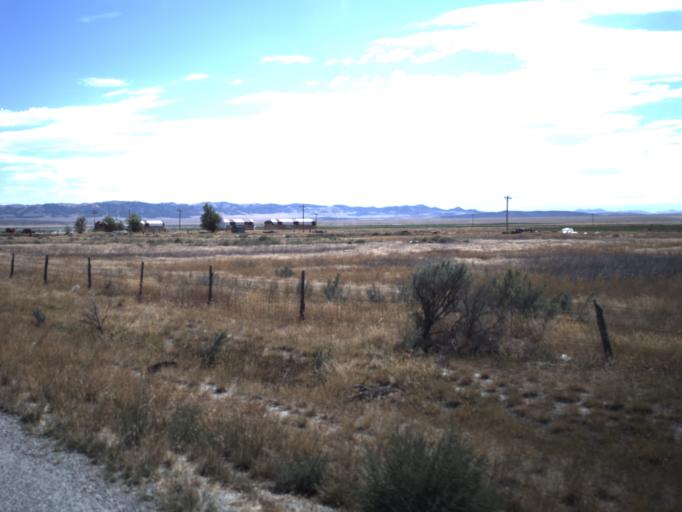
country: US
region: Idaho
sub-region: Oneida County
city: Malad City
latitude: 41.9666
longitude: -112.9068
